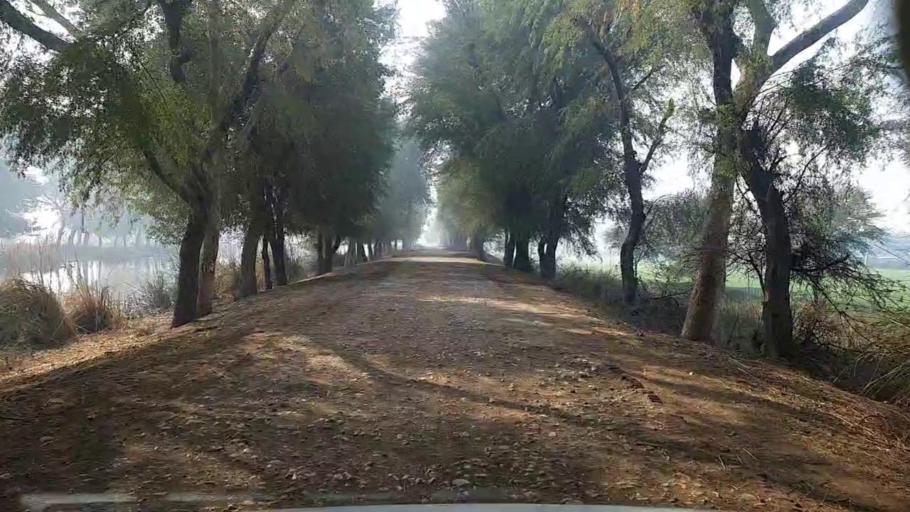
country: PK
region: Sindh
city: Khairpur
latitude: 27.9538
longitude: 69.6529
